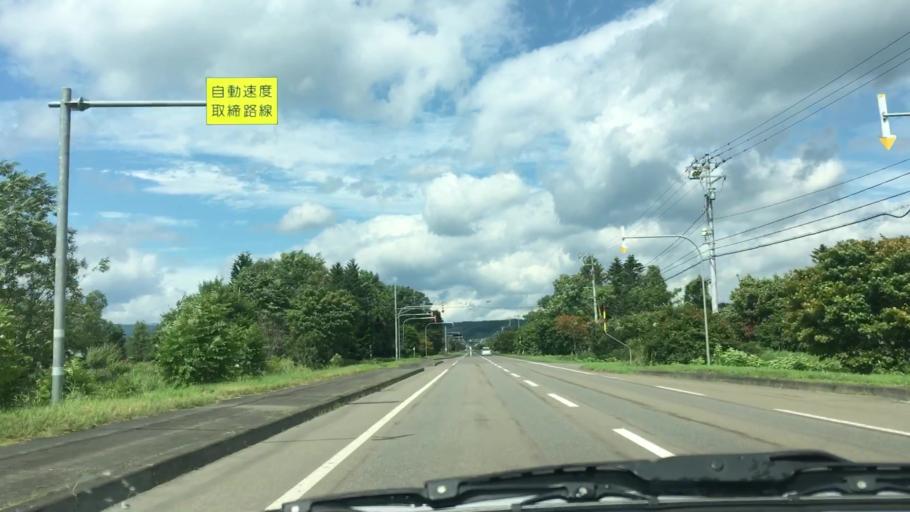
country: JP
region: Hokkaido
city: Otofuke
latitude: 43.2936
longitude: 143.3088
